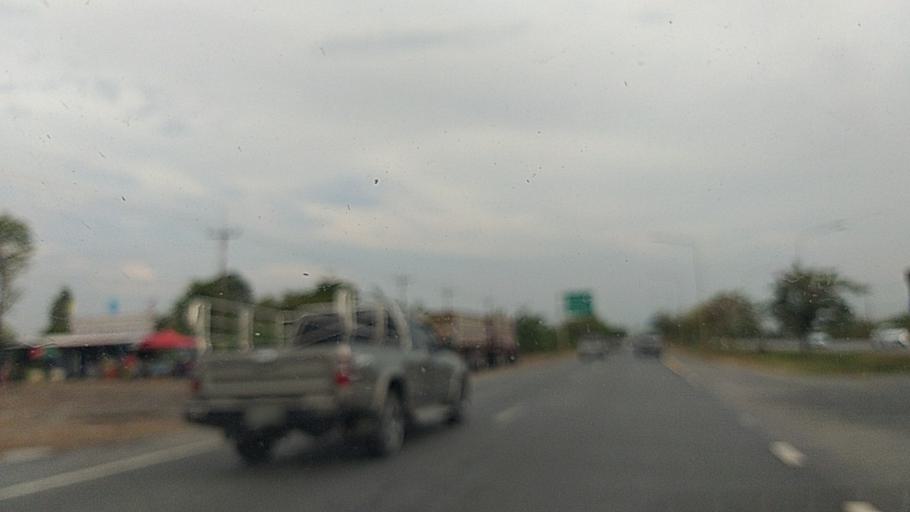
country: TH
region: Phra Nakhon Si Ayutthaya
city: Bang Pa-in
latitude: 14.2272
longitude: 100.5404
